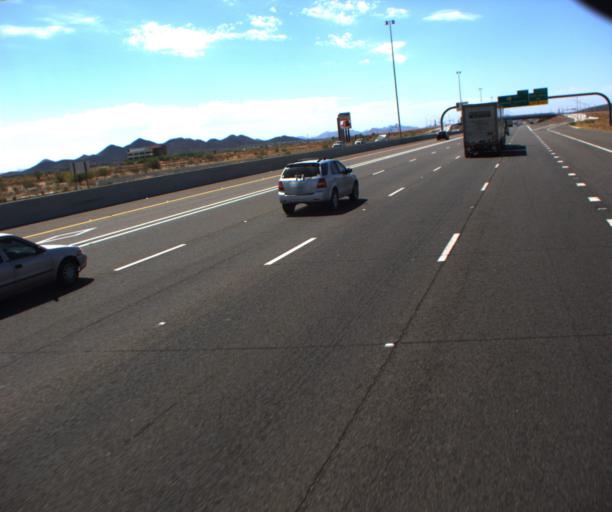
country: US
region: Arizona
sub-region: Maricopa County
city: Anthem
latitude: 33.7914
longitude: -112.1342
